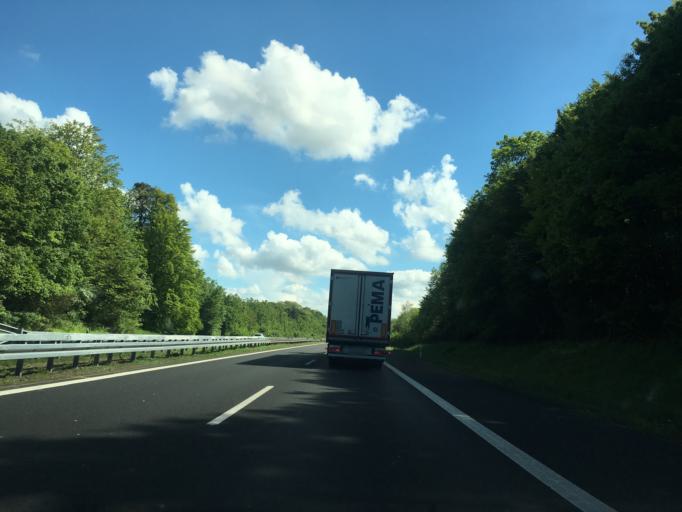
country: DE
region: Bavaria
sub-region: Regierungsbezirk Unterfranken
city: Unterpleichfeld
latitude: 49.9050
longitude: 10.0000
